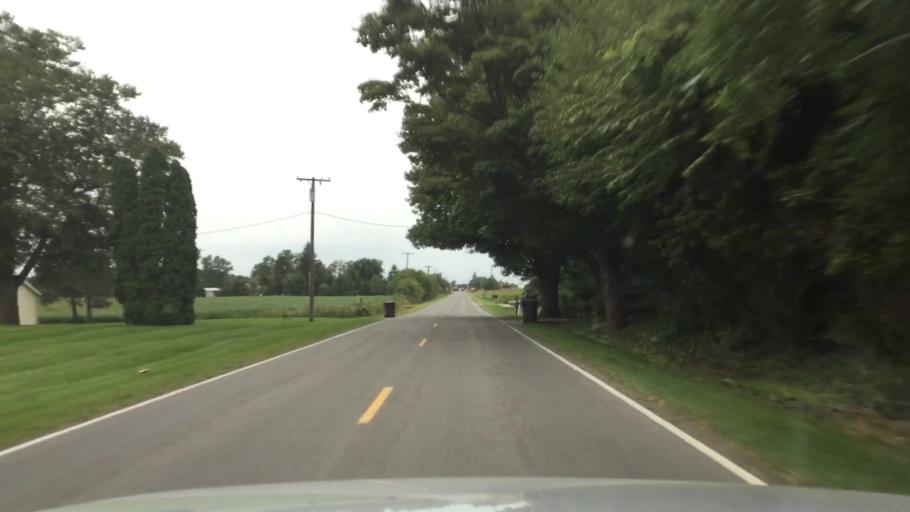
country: US
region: Michigan
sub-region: Washtenaw County
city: Milan
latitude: 42.1132
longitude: -83.6877
